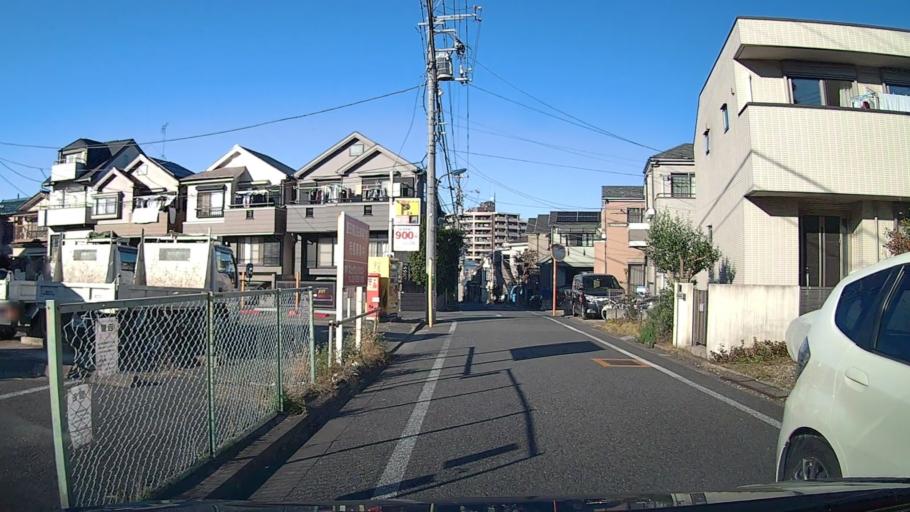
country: JP
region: Saitama
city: Wako
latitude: 35.7548
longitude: 139.5960
